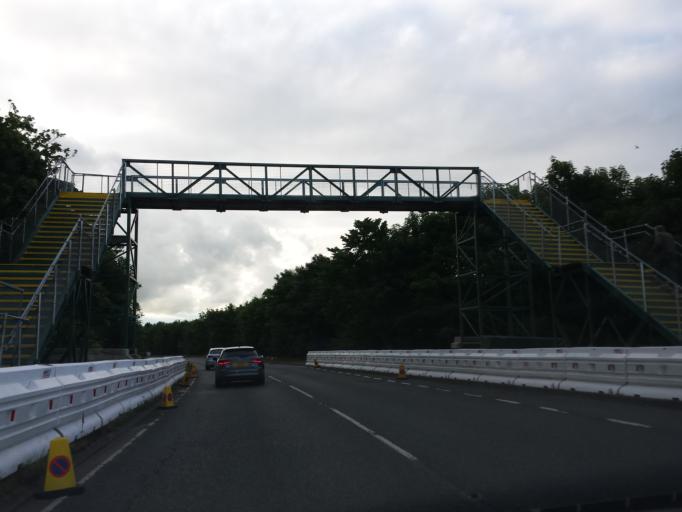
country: GB
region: Scotland
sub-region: Fife
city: Saint Andrews
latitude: 56.3461
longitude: -2.8192
